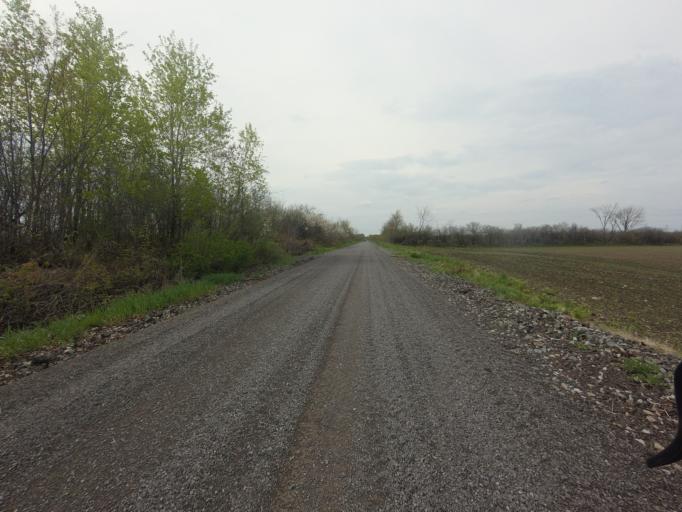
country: CA
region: Ontario
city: Carleton Place
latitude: 45.1934
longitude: -76.1635
